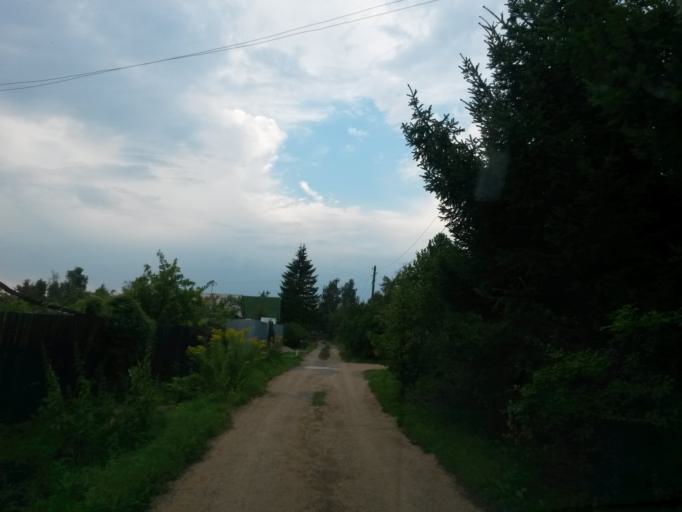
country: RU
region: Jaroslavl
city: Yaroslavl
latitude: 57.6090
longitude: 39.7850
